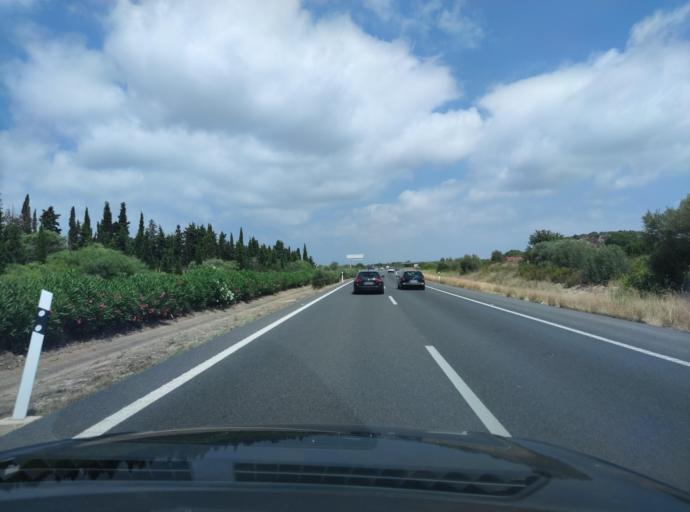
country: ES
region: Valencia
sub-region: Provincia de Castello
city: Vinaros
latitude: 40.4850
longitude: 0.4165
